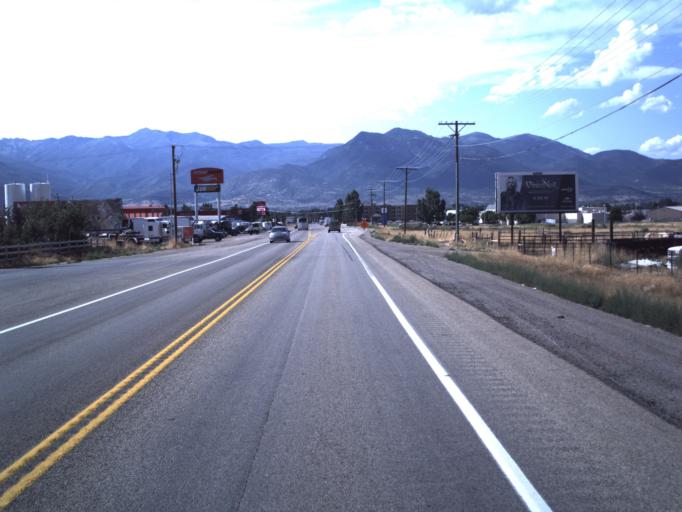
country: US
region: Utah
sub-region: Wasatch County
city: Heber
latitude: 40.4865
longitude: -111.4066
